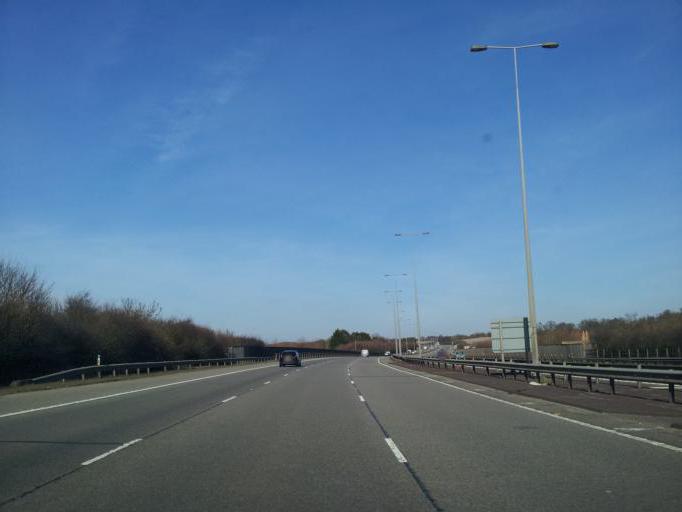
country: GB
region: England
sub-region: Cambridgeshire
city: Great Stukeley
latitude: 52.3635
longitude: -0.2555
